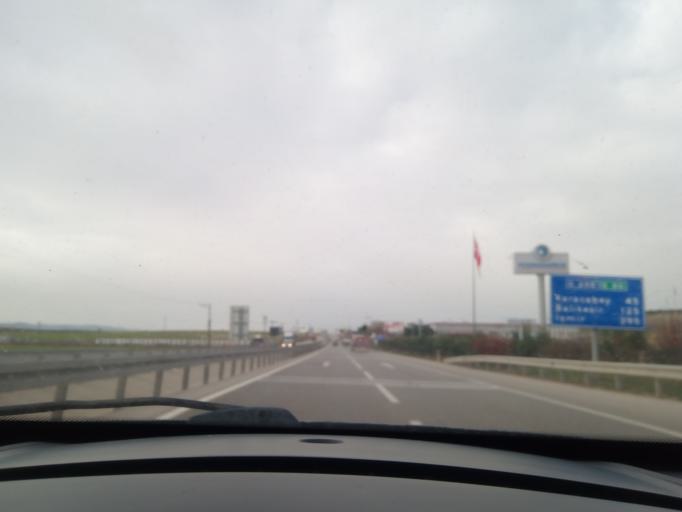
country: TR
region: Bursa
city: Gorukle
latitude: 40.2220
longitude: 28.7723
